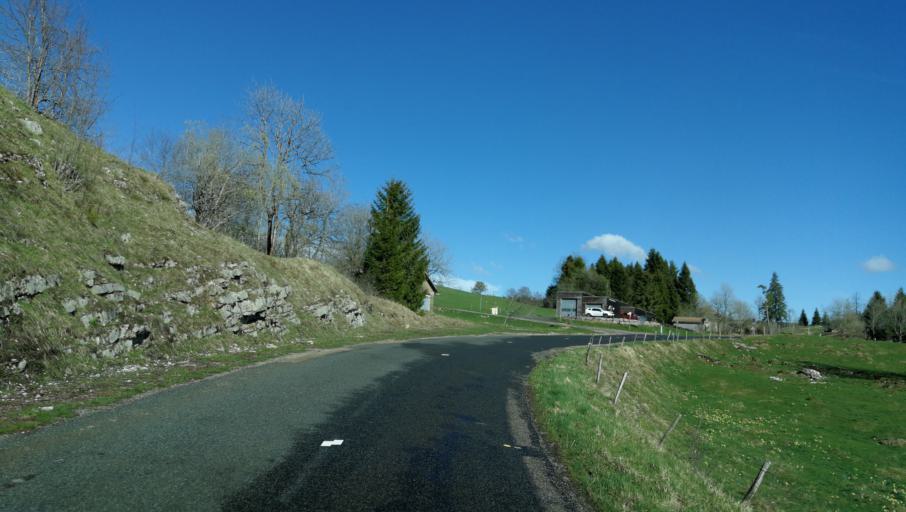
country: FR
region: Franche-Comte
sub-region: Departement du Jura
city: Saint-Claude
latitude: 46.3060
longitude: 5.8385
